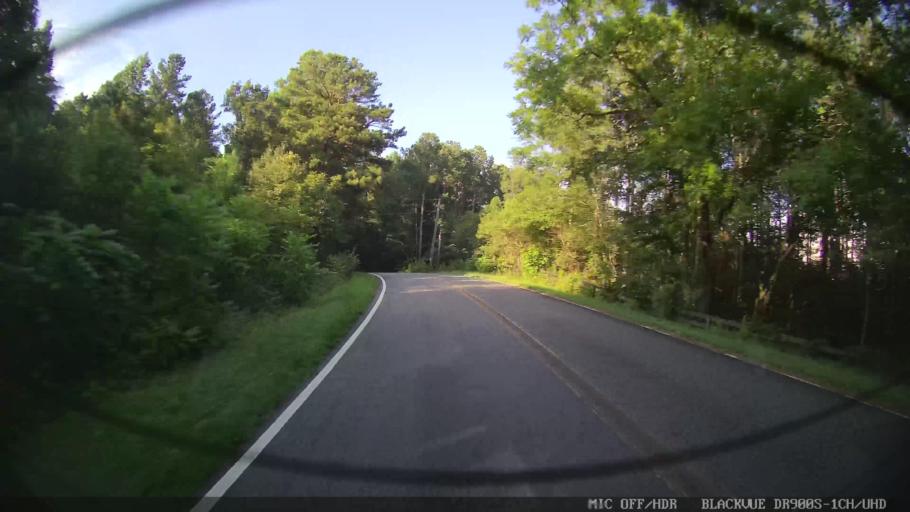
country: US
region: Georgia
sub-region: Bartow County
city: Emerson
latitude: 34.2010
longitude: -84.6930
